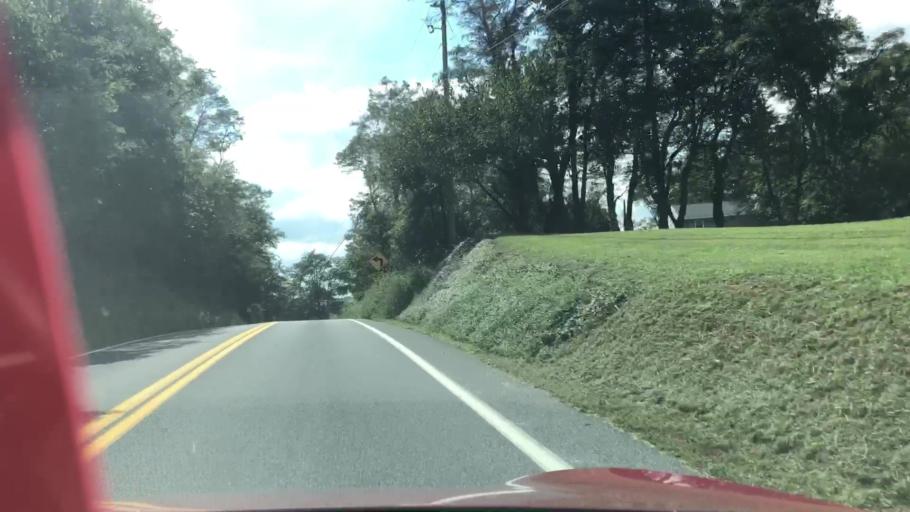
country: US
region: Pennsylvania
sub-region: Dauphin County
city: Skyline View
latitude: 40.3533
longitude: -76.6724
